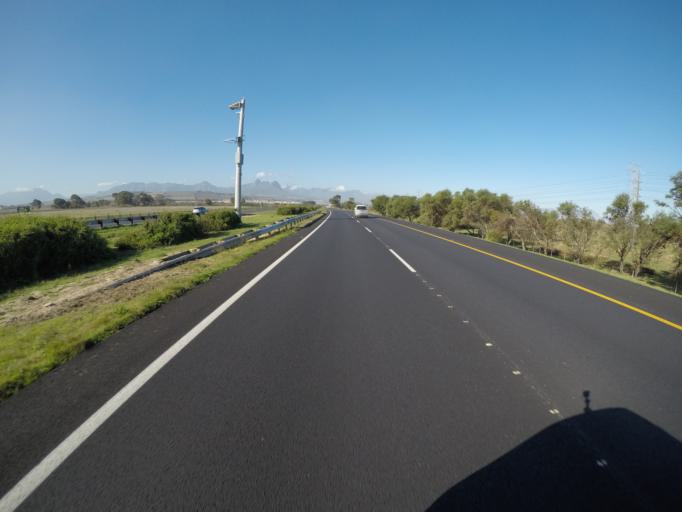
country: ZA
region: Western Cape
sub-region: Cape Winelands District Municipality
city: Stellenbosch
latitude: -34.0429
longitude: 18.7332
